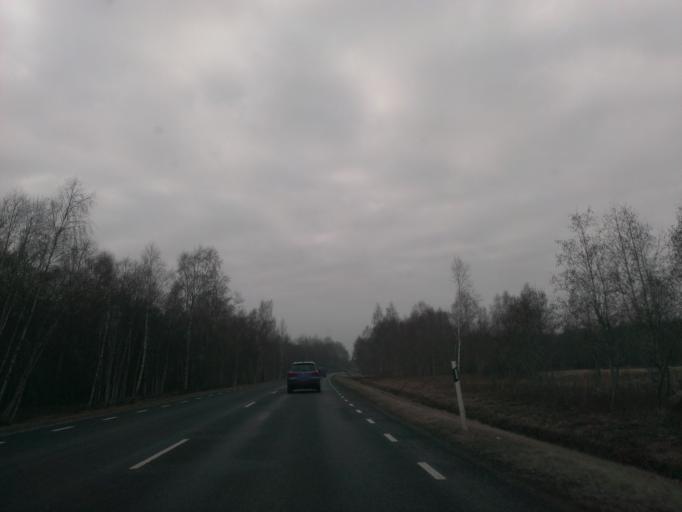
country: EE
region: Saare
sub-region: Orissaare vald
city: Orissaare
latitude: 58.6053
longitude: 23.2508
